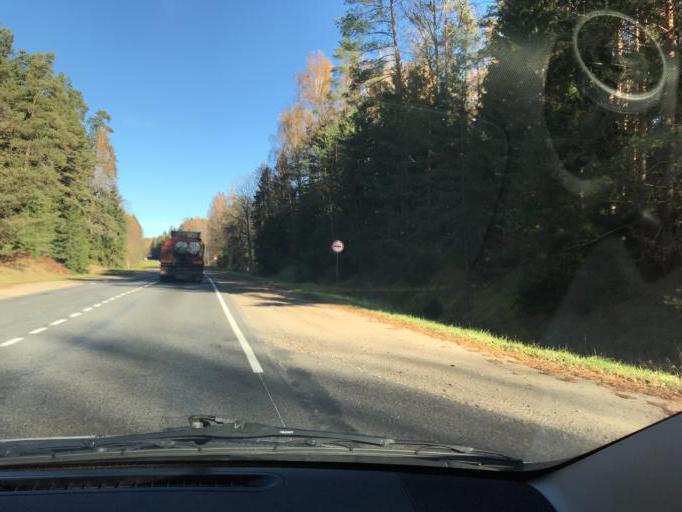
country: BY
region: Vitebsk
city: Polatsk
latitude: 55.3575
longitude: 28.8050
